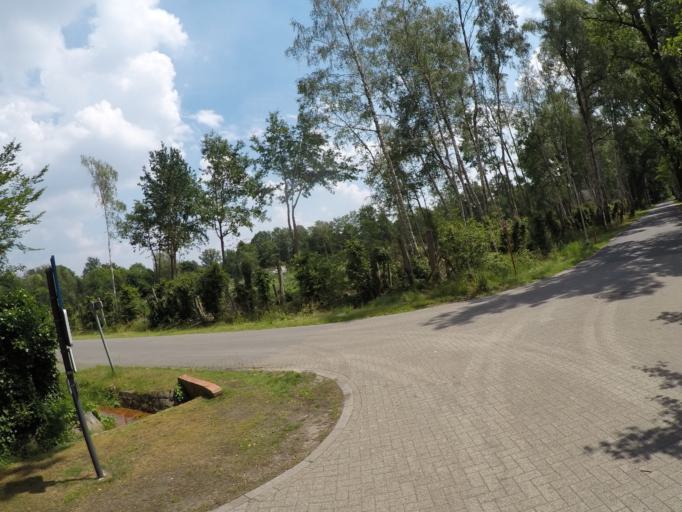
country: BE
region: Flanders
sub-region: Provincie Antwerpen
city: Schilde
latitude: 51.2638
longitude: 4.5990
